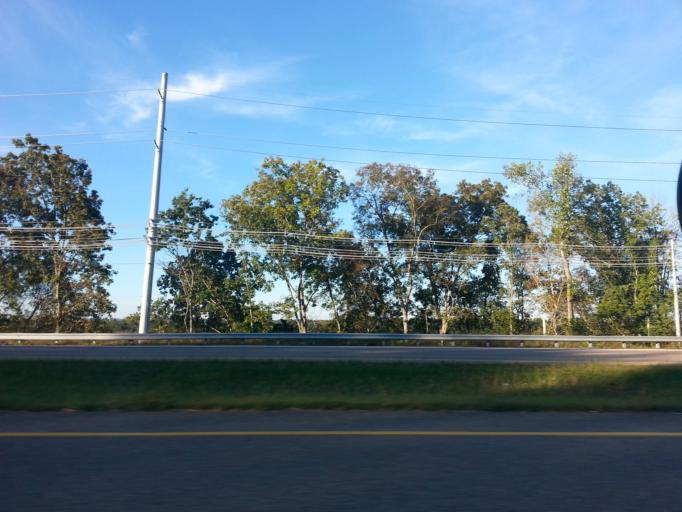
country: US
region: Tennessee
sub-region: Blount County
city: Wildwood
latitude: 35.7573
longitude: -83.8547
